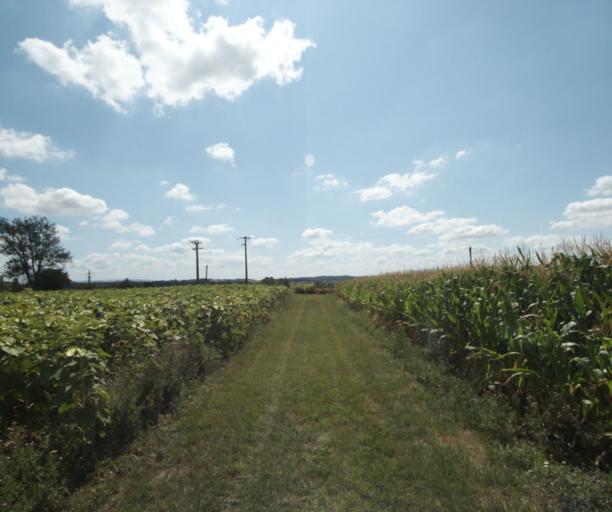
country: FR
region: Midi-Pyrenees
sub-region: Departement de la Haute-Garonne
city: Auriac-sur-Vendinelle
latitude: 43.4529
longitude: 1.8018
